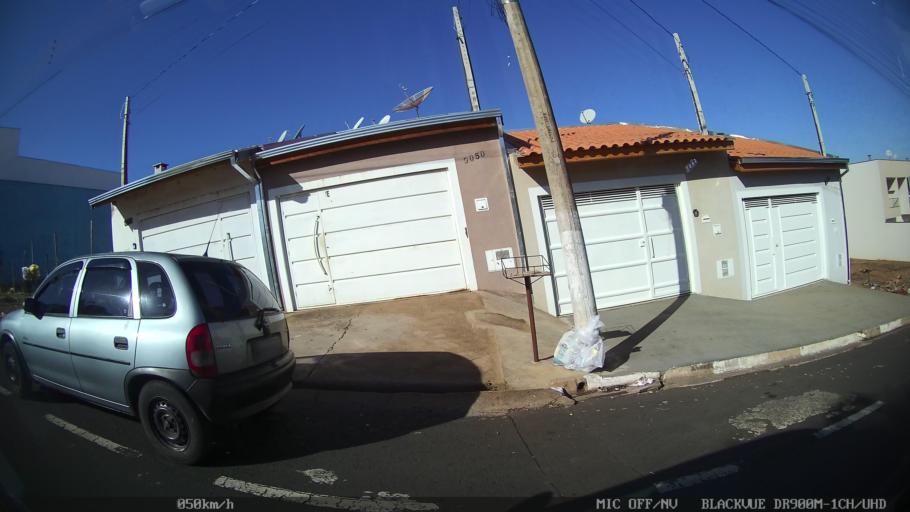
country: BR
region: Sao Paulo
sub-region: Franca
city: Franca
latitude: -20.4868
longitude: -47.4286
